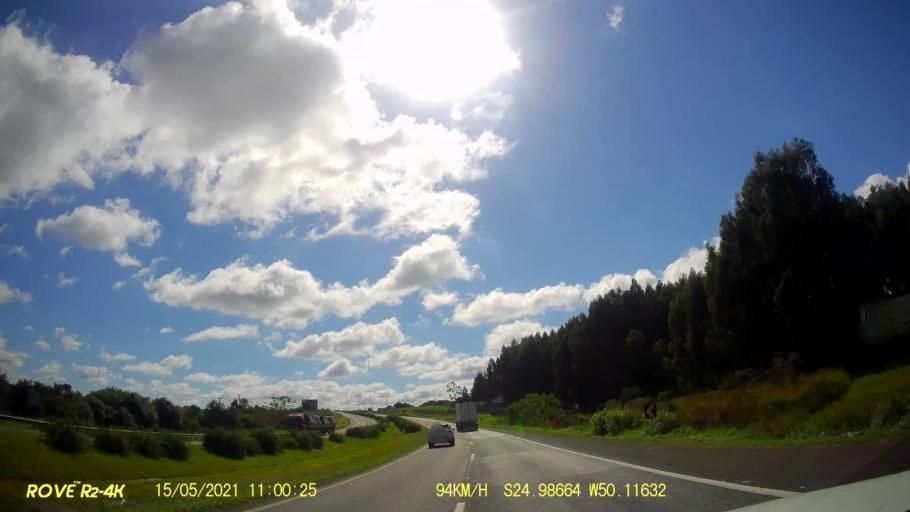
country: BR
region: Parana
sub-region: Carambei
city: Carambei
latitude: -24.9869
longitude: -50.1160
